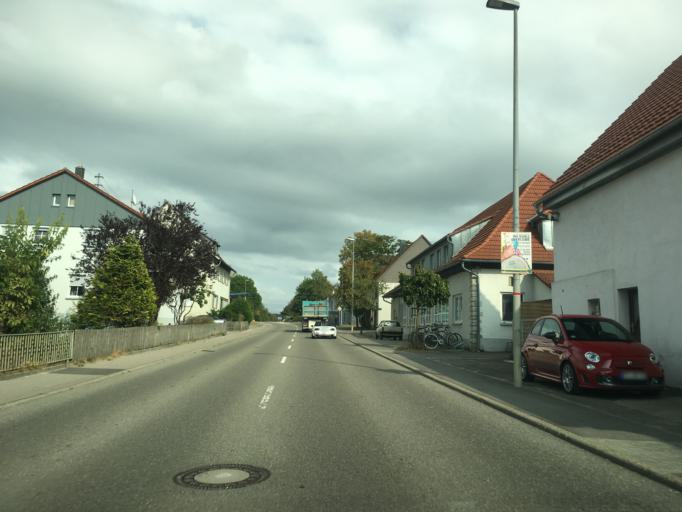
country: DE
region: Baden-Wuerttemberg
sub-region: Tuebingen Region
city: Pfullingen
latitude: 48.4080
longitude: 9.1908
